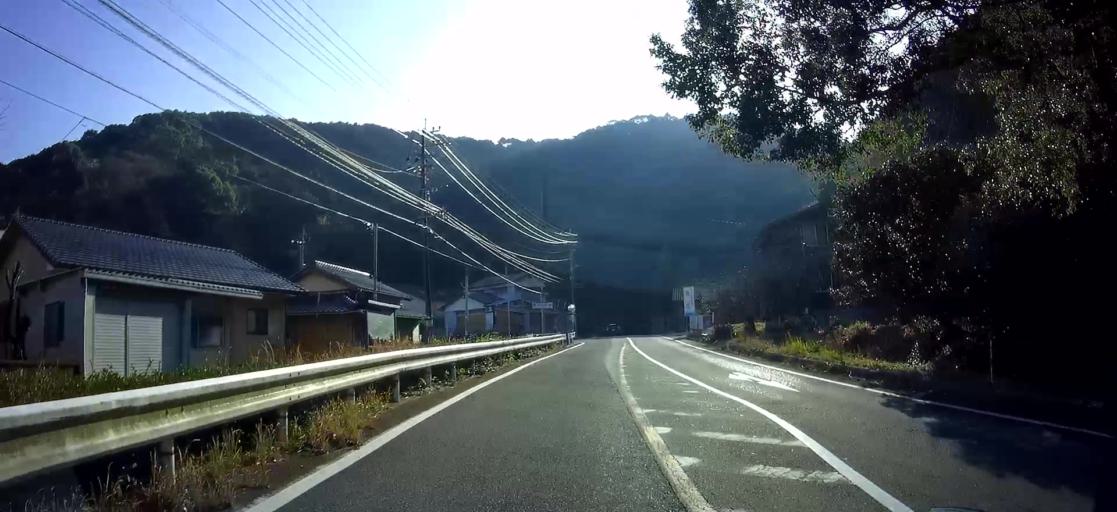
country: JP
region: Kumamoto
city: Hondo
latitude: 32.4339
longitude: 130.4059
